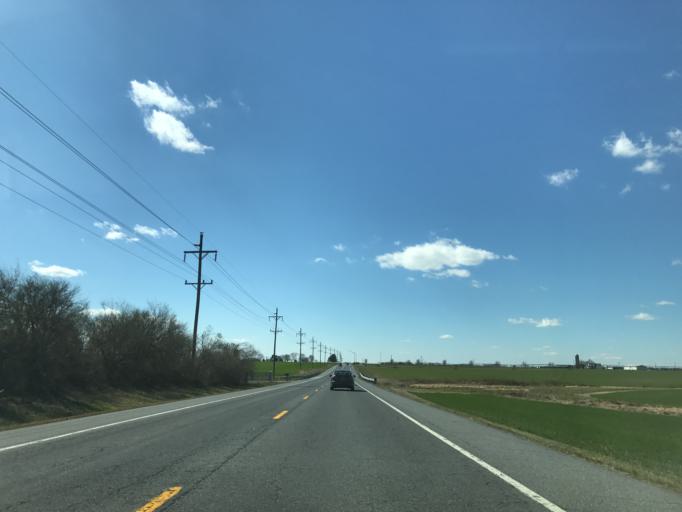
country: US
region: Maryland
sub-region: Queen Anne's County
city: Kingstown
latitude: 39.2627
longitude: -75.9080
